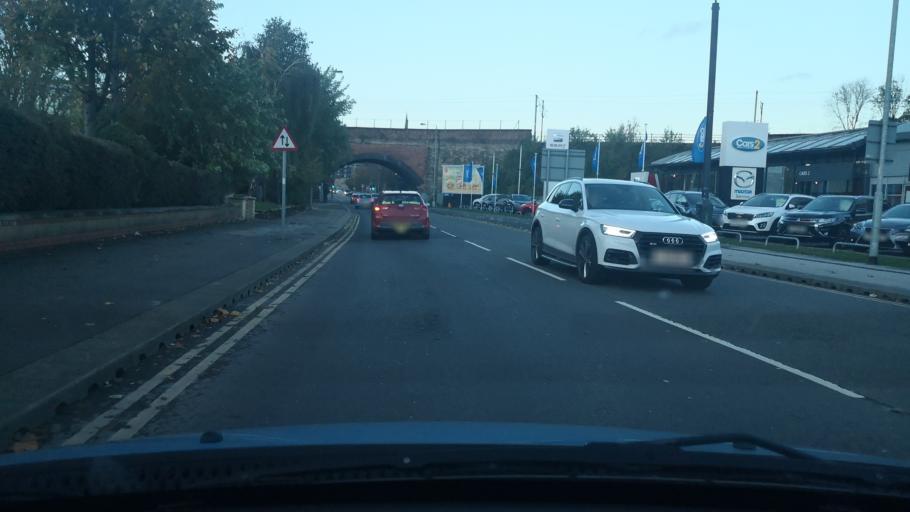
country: GB
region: England
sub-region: City and Borough of Wakefield
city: Wakefield
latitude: 53.6765
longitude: -1.5011
